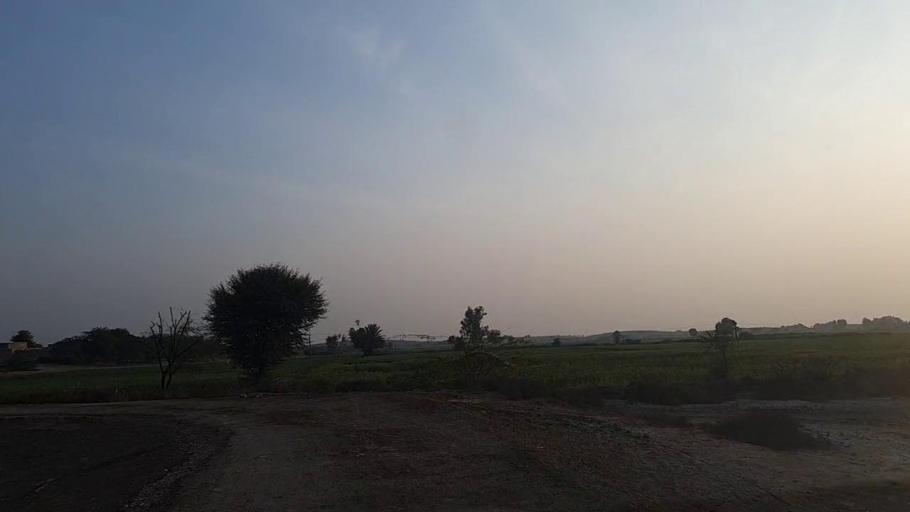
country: PK
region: Sindh
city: Jam Sahib
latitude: 26.4098
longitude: 68.6056
